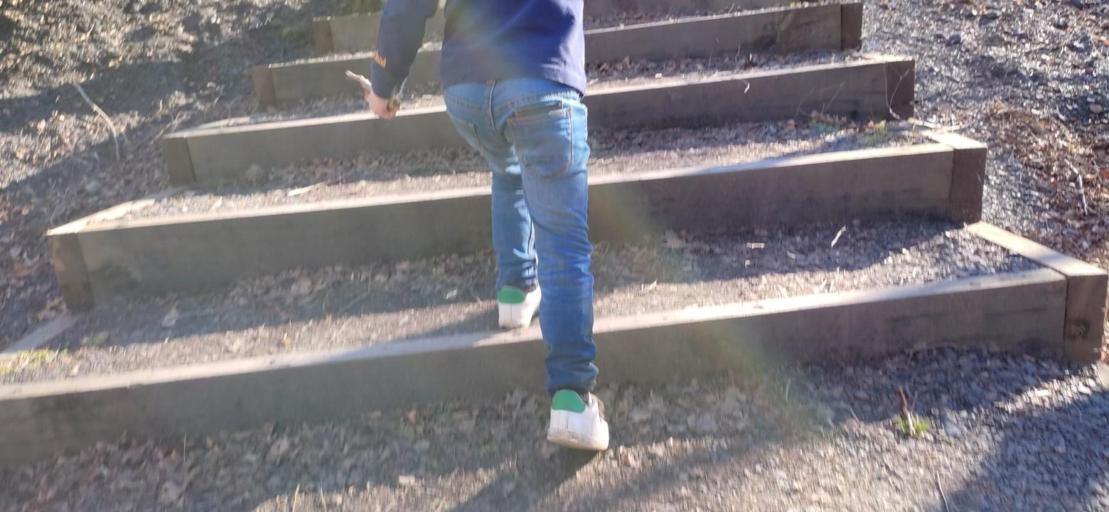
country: FR
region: Nord-Pas-de-Calais
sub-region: Departement du Pas-de-Calais
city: Oignies
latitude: 50.4820
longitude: 2.9910
